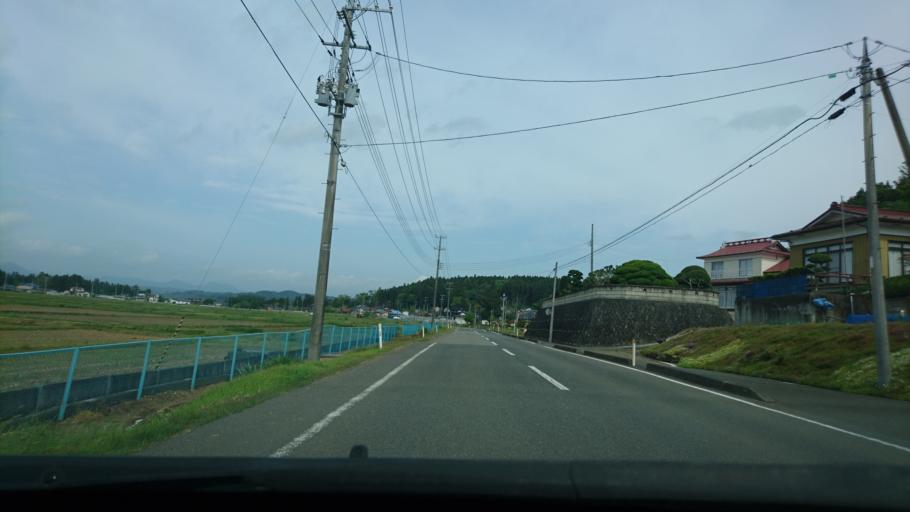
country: JP
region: Iwate
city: Ichinoseki
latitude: 38.8256
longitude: 141.0307
